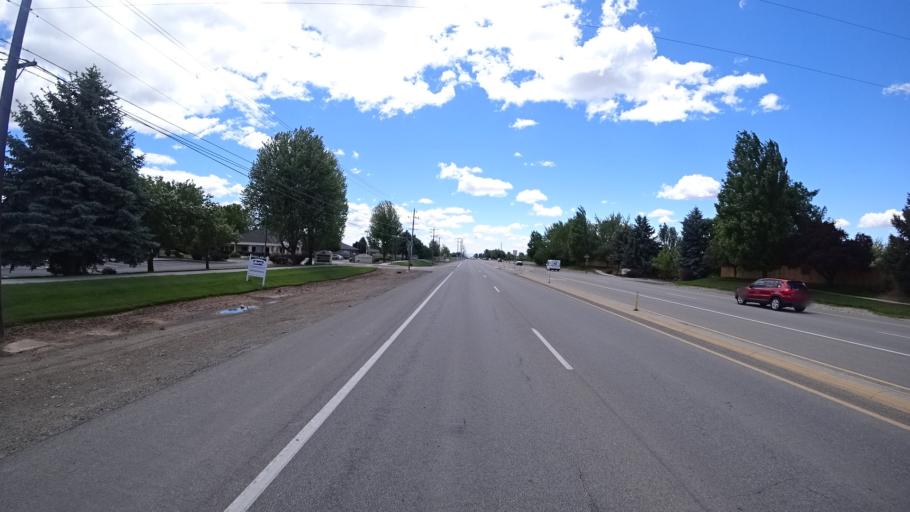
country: US
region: Idaho
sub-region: Ada County
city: Eagle
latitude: 43.6536
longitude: -116.3541
